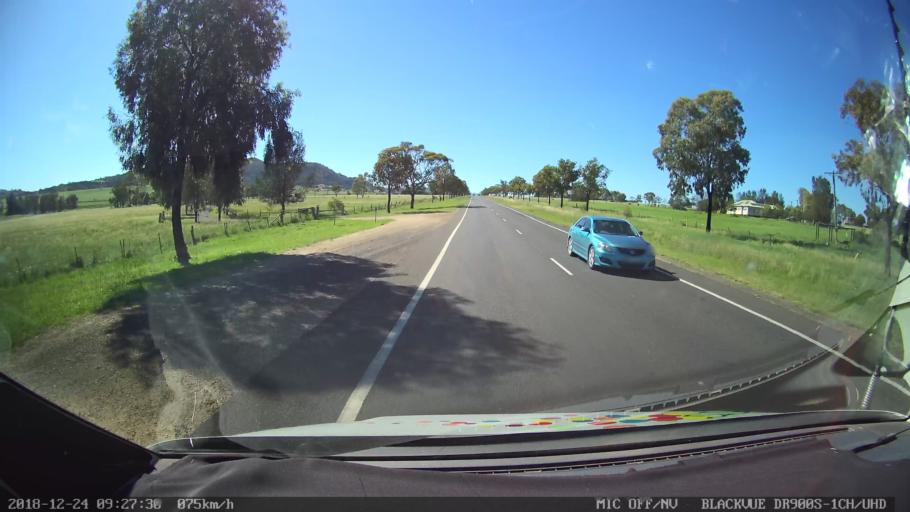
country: AU
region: New South Wales
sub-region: Liverpool Plains
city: Quirindi
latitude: -31.5287
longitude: 150.6816
